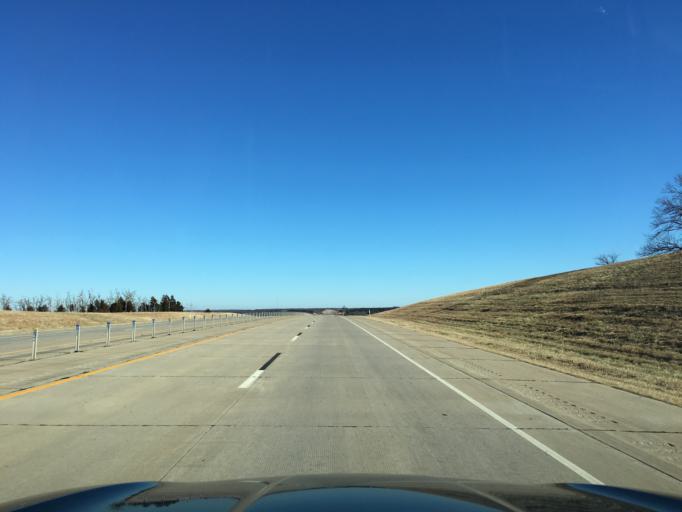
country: US
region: Oklahoma
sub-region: Payne County
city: Yale
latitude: 36.2251
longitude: -96.6407
